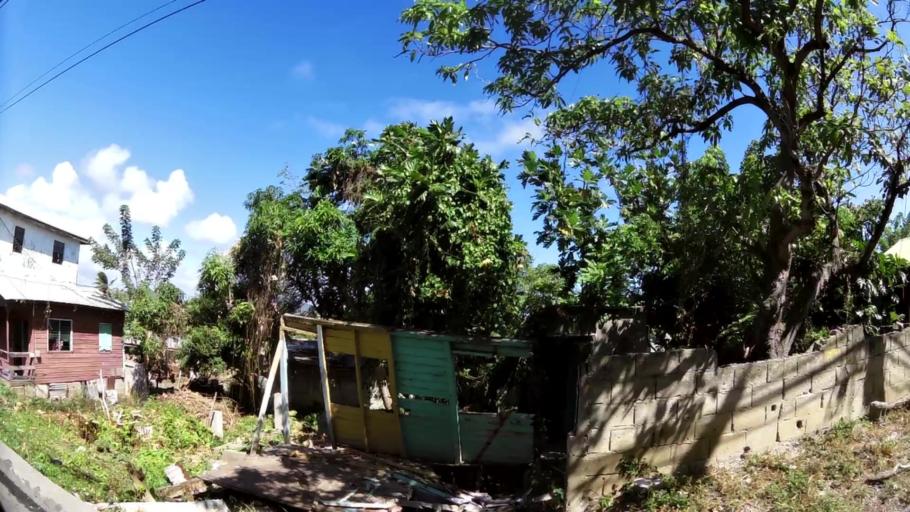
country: LC
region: Vieux-Fort
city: Vieux Fort
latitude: 13.7263
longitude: -60.9536
